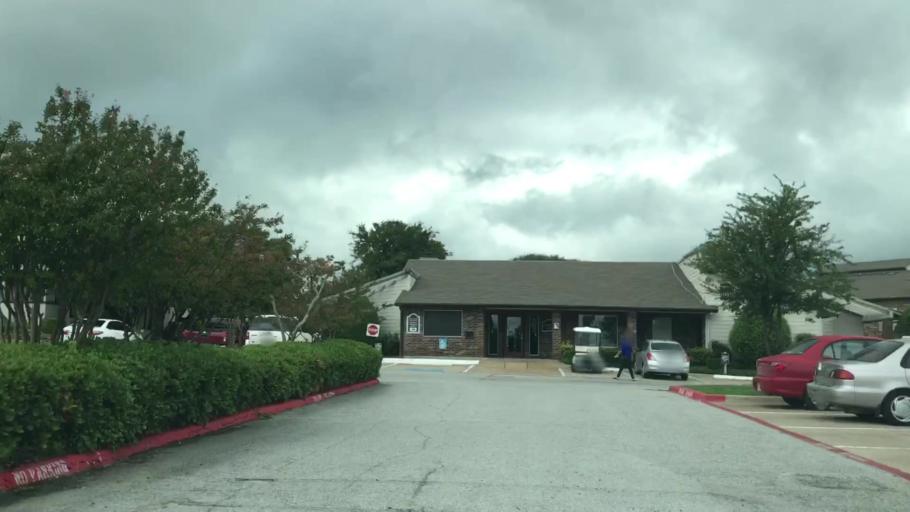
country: US
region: Texas
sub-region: Dallas County
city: Garland
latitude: 32.8825
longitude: -96.6175
